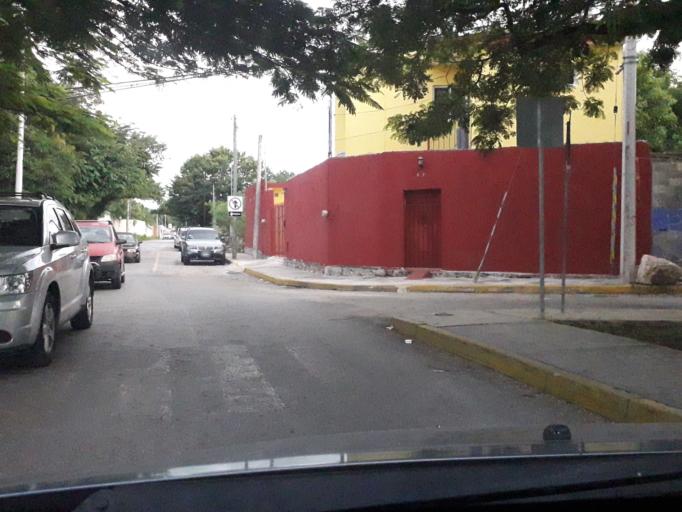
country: MX
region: Yucatan
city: Merida
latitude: 21.0196
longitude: -89.6351
